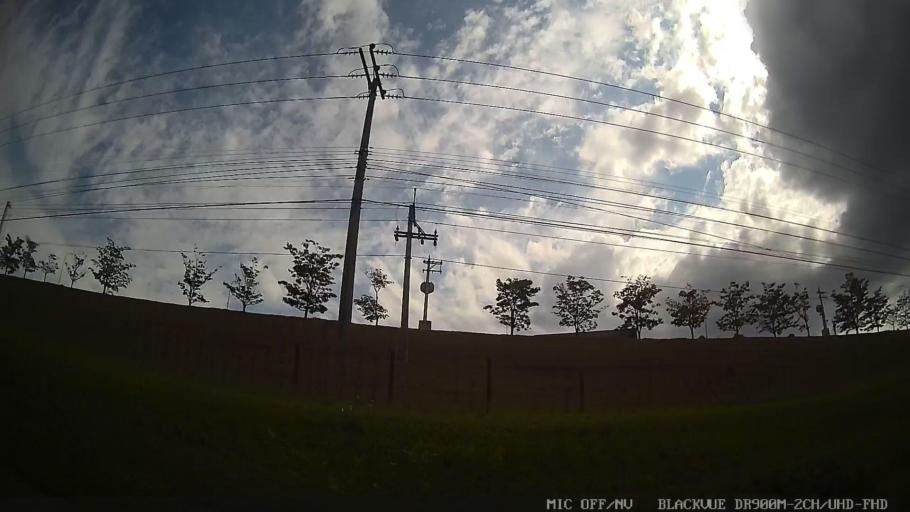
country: BR
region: Sao Paulo
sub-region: Indaiatuba
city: Indaiatuba
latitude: -23.1397
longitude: -47.2458
